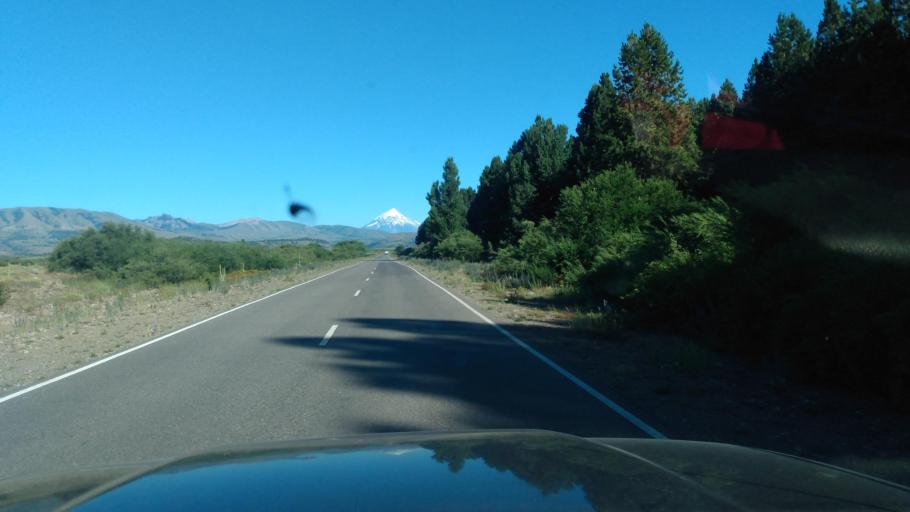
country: AR
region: Neuquen
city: Junin de los Andes
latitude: -39.8968
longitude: -71.1446
